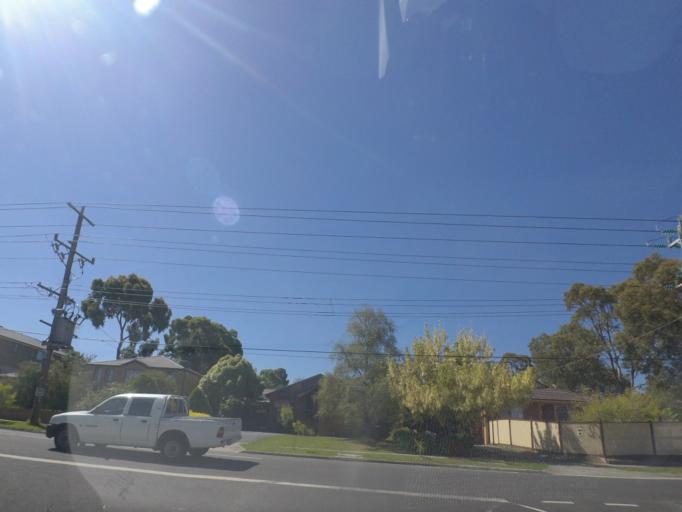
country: AU
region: Victoria
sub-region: Manningham
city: Park Orchards
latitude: -37.7927
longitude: 145.2243
